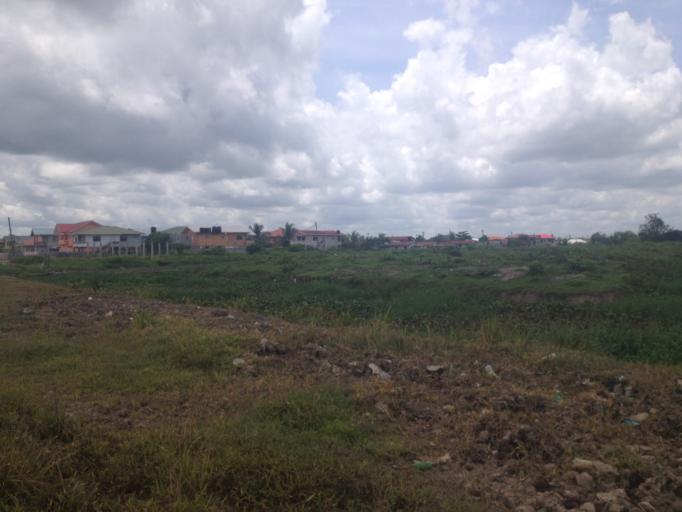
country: GY
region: Demerara-Mahaica
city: Georgetown
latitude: 6.7086
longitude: -58.1866
